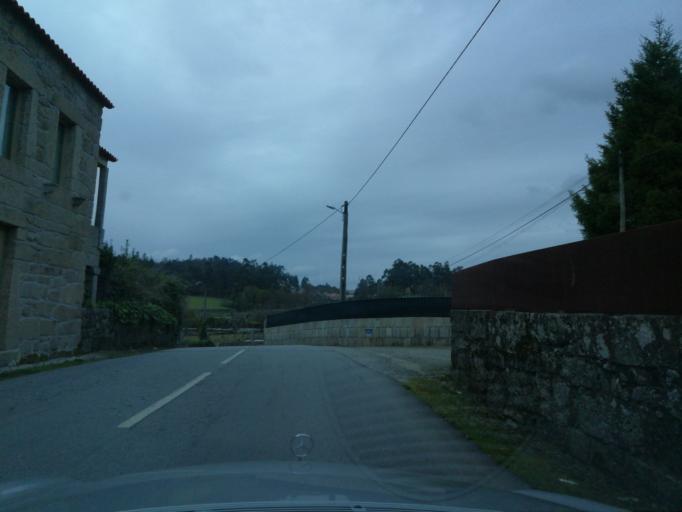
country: PT
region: Braga
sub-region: Braga
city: Oliveira
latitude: 41.4831
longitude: -8.4710
